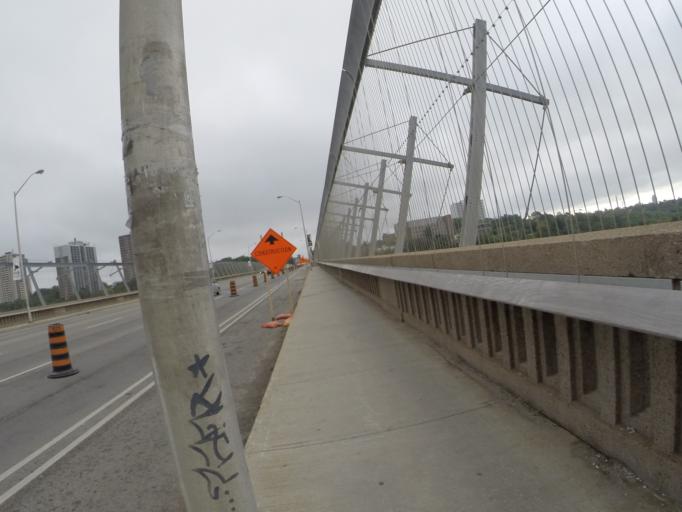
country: CA
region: Ontario
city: Toronto
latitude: 43.6745
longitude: -79.3667
